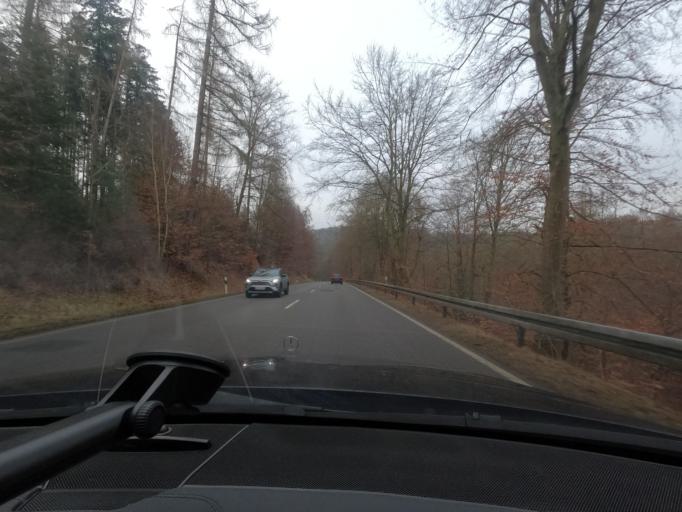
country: DE
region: Hesse
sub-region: Regierungsbezirk Kassel
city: Bad Arolsen
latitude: 51.3715
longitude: 9.0370
